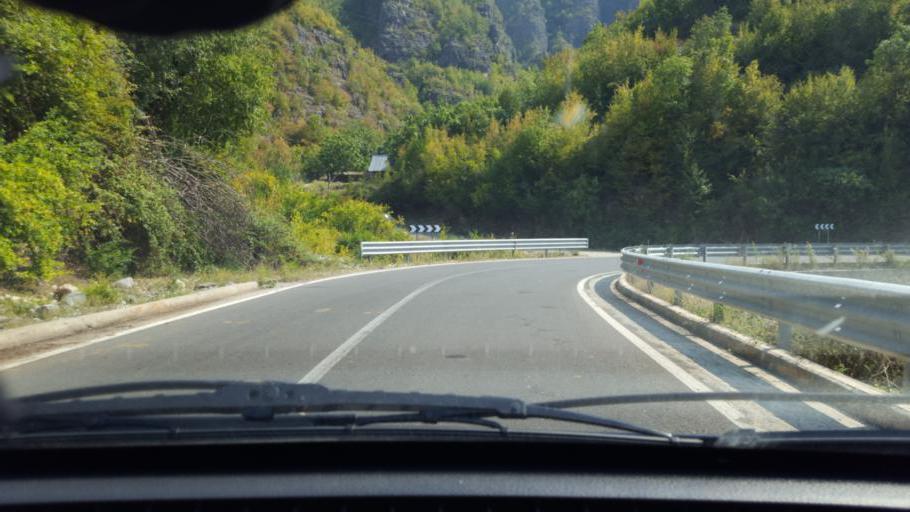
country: AL
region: Shkoder
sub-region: Rrethi i Malesia e Madhe
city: Kastrat
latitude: 42.4290
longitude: 19.5336
